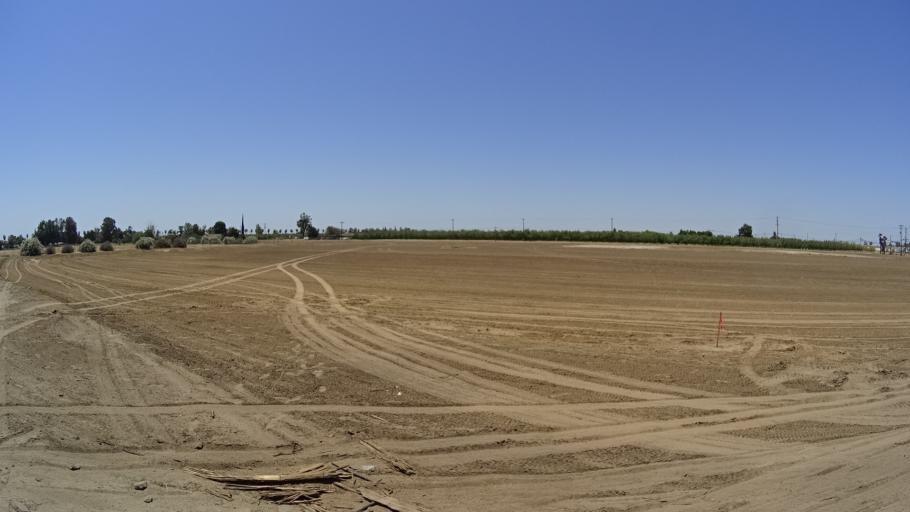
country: US
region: California
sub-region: Fresno County
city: West Park
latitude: 36.7344
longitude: -119.8334
